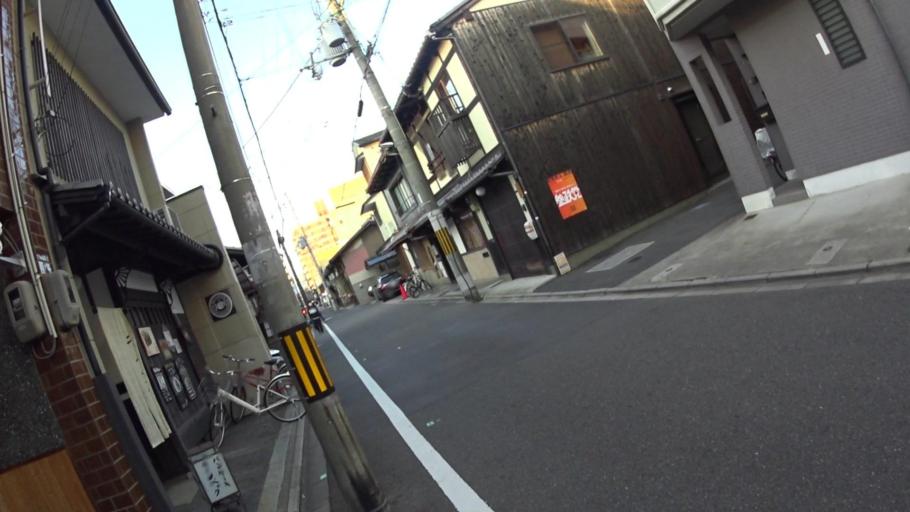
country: JP
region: Kyoto
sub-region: Kyoto-shi
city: Kamigyo-ku
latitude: 35.0276
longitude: 135.7490
